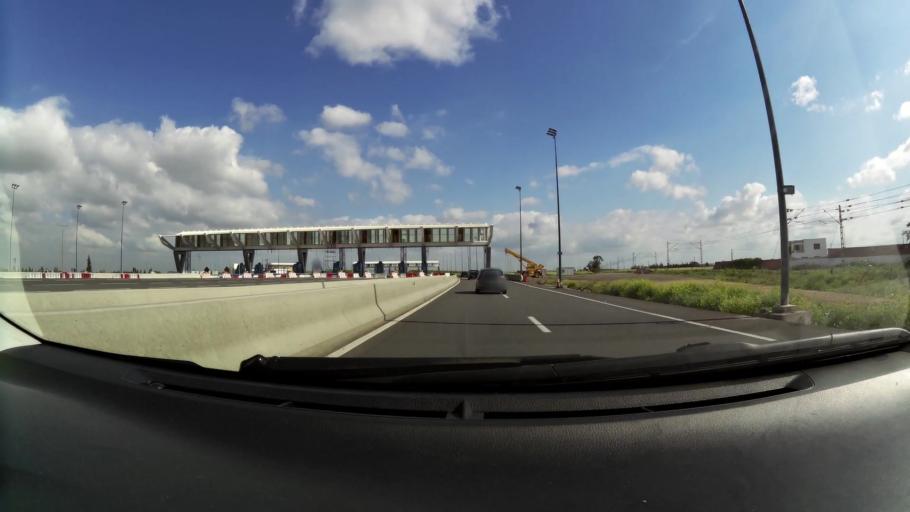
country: MA
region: Chaouia-Ouardigha
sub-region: Settat Province
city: Berrechid
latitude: 33.3209
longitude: -7.6053
